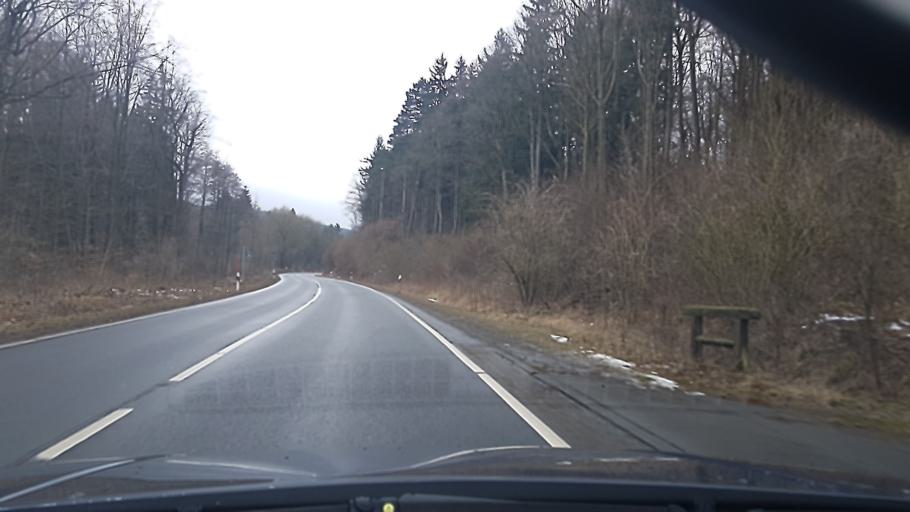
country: DE
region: Lower Saxony
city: Goslar
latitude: 51.8971
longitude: 10.4120
